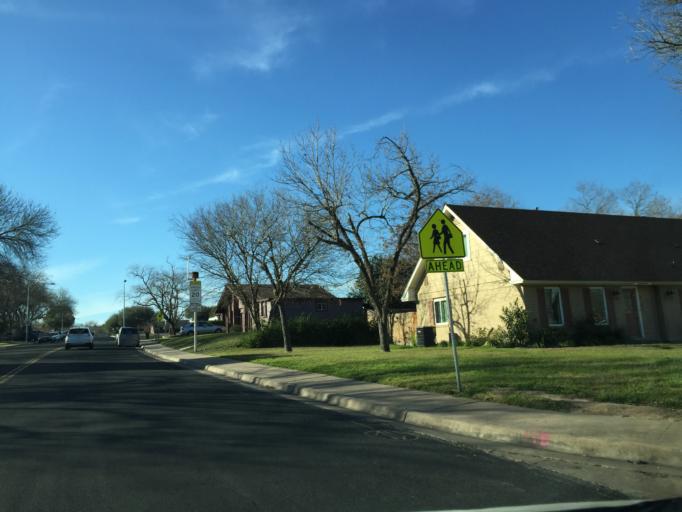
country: US
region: Texas
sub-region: Travis County
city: Onion Creek
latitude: 30.2041
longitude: -97.7872
